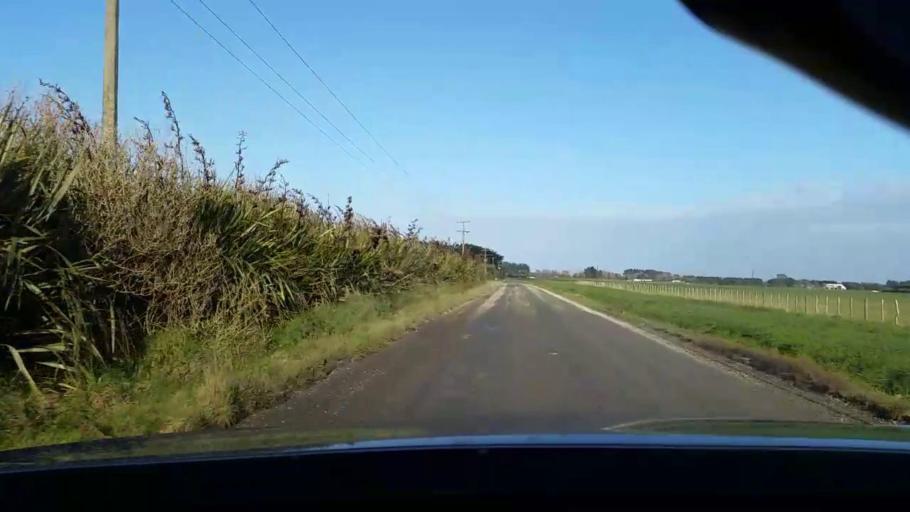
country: NZ
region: Southland
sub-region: Invercargill City
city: Invercargill
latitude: -46.3048
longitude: 168.3034
